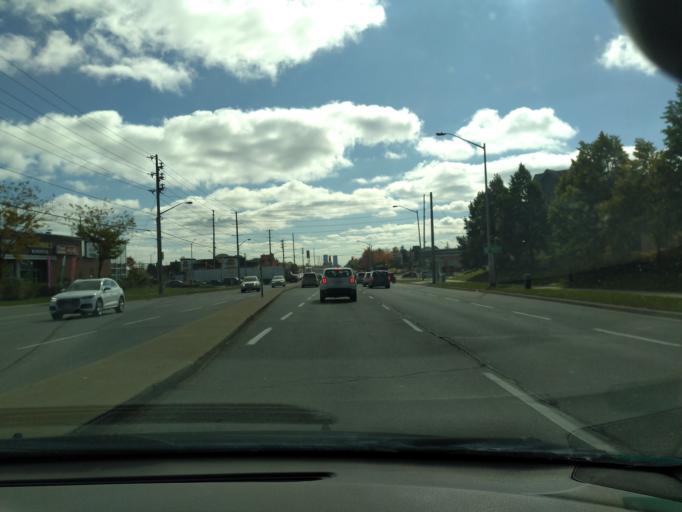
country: CA
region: Ontario
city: Vaughan
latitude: 43.8273
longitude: -79.5566
